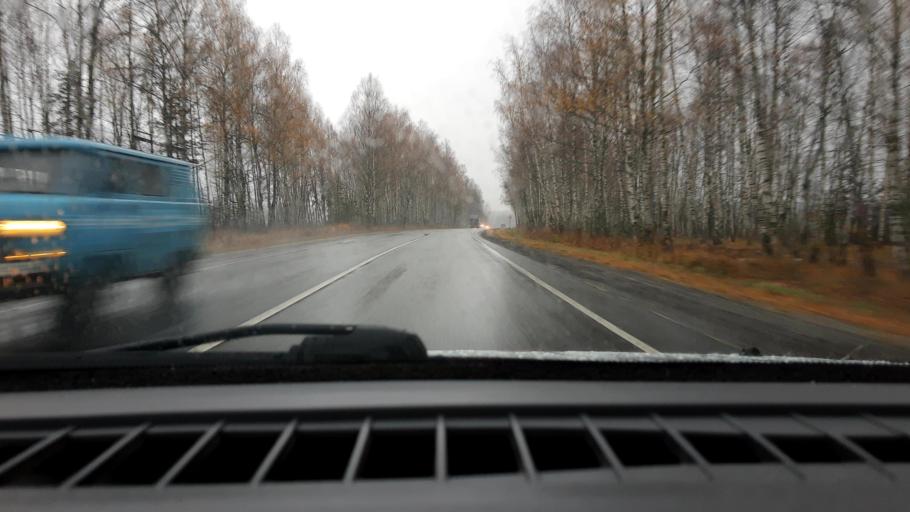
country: RU
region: Nizjnij Novgorod
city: Linda
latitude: 56.6724
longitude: 44.1425
